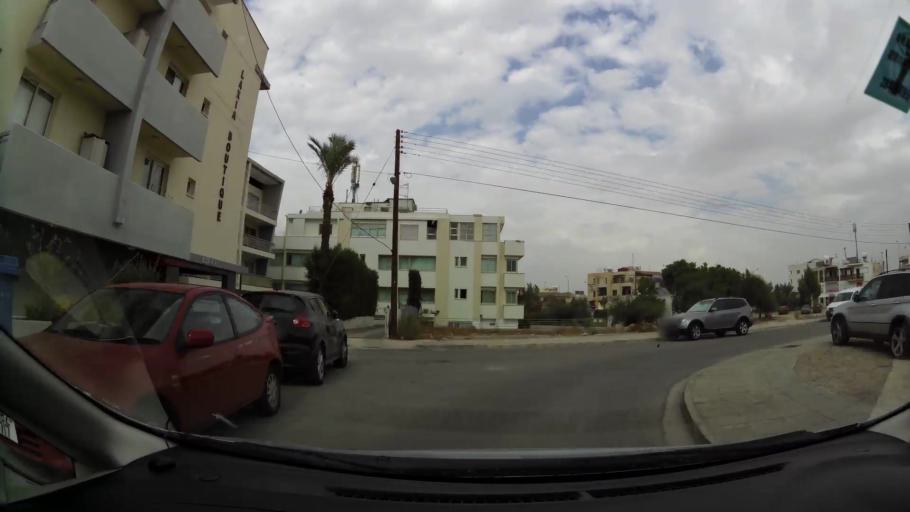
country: CY
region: Lefkosia
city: Geri
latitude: 35.1055
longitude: 33.3776
